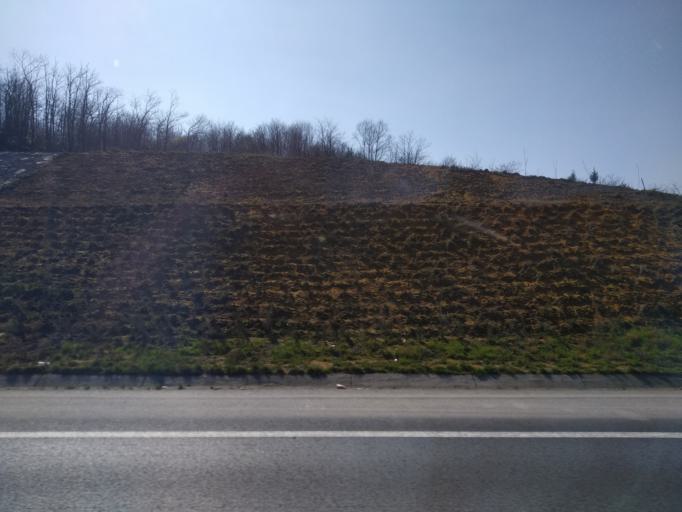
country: TR
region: Istanbul
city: Mahmut Sevket Pasa
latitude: 41.1685
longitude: 29.2511
